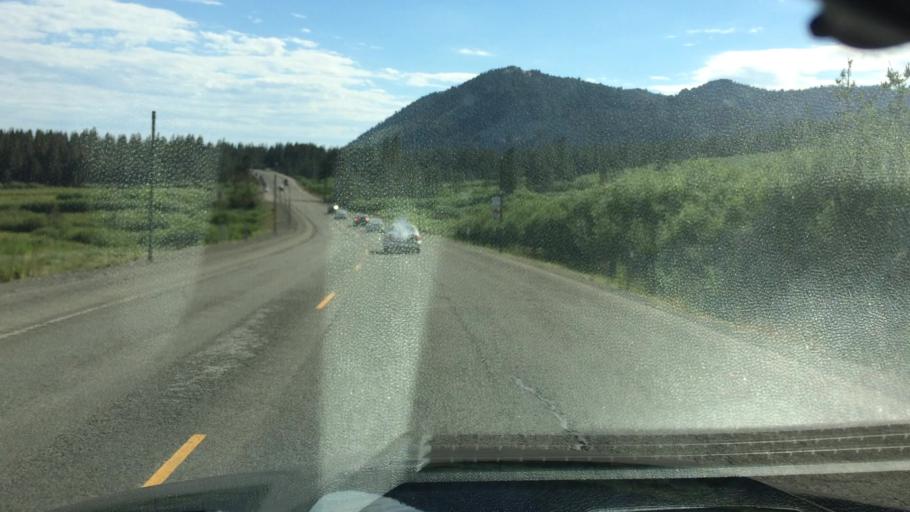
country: US
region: Nevada
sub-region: Washoe County
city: Incline Village
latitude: 39.3048
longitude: -119.9150
